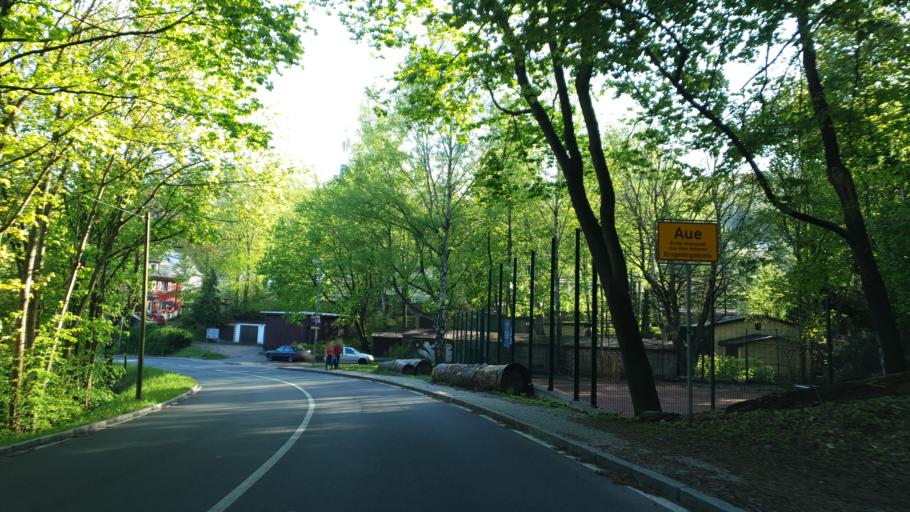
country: DE
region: Saxony
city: Schlema
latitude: 50.5962
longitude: 12.6894
